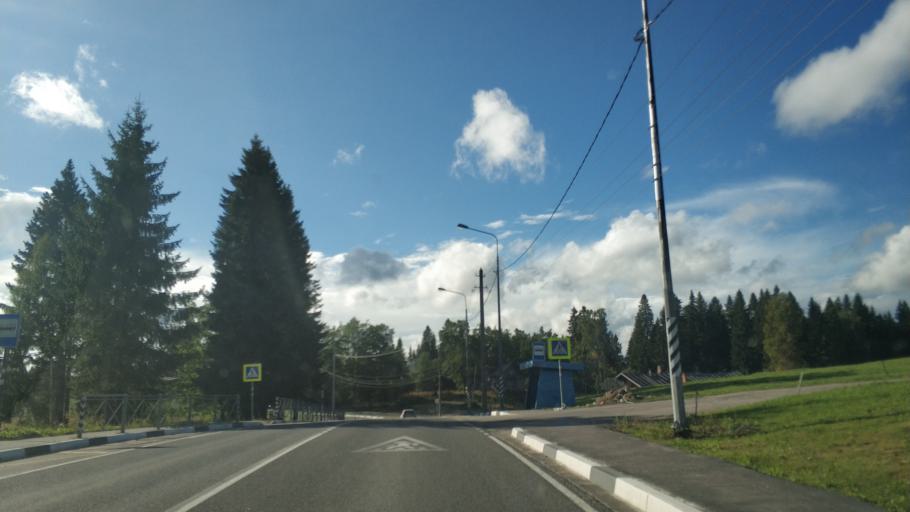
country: RU
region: Republic of Karelia
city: Lakhdenpokh'ya
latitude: 61.5226
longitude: 30.1847
